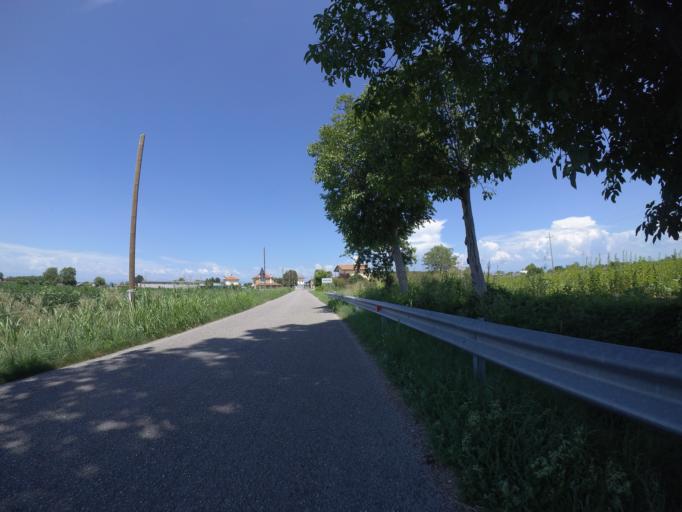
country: IT
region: Friuli Venezia Giulia
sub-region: Provincia di Udine
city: Talmassons
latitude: 45.9201
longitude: 13.1192
